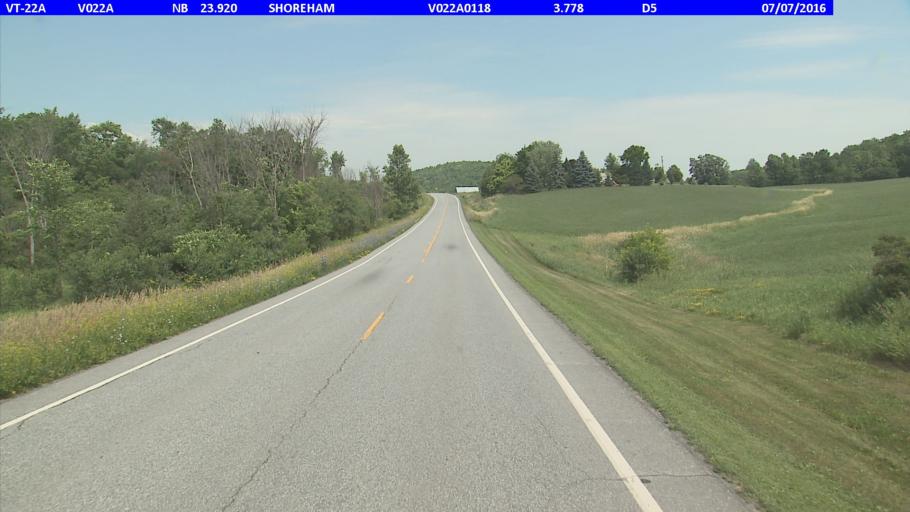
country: US
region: New York
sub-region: Essex County
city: Ticonderoga
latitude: 43.9040
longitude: -73.3082
